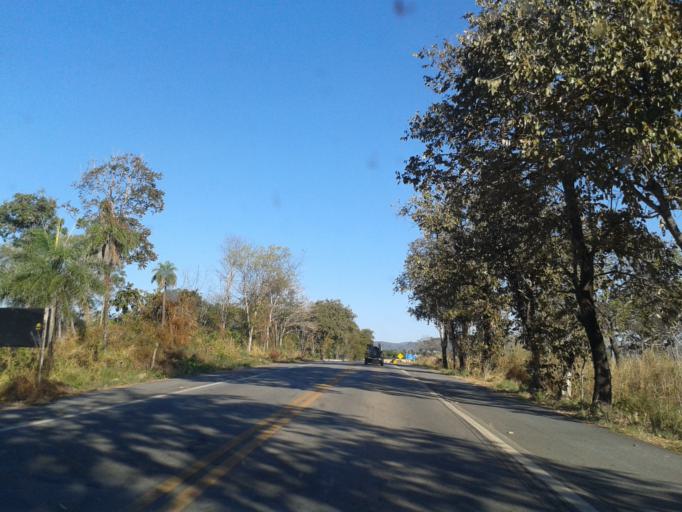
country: BR
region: Goias
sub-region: Itapuranga
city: Itapuranga
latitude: -15.4337
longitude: -50.3713
